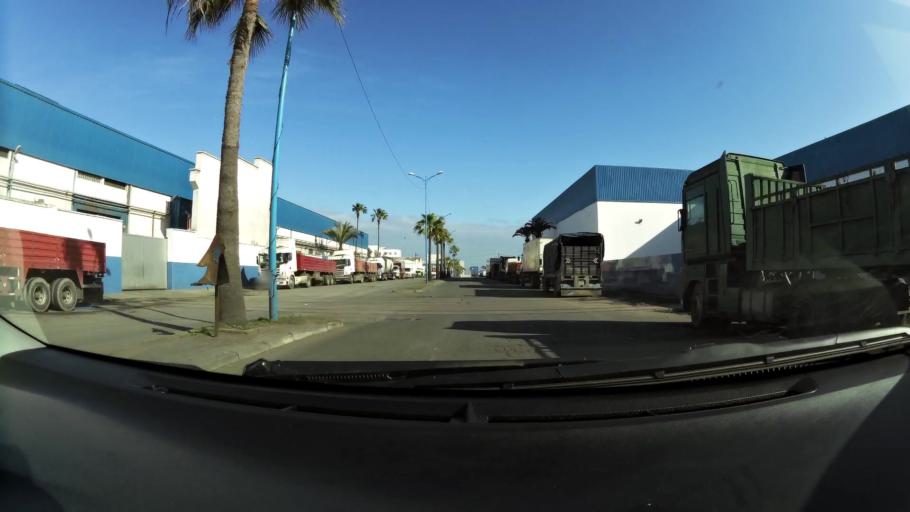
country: MA
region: Grand Casablanca
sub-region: Casablanca
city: Casablanca
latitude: 33.6032
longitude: -7.5741
